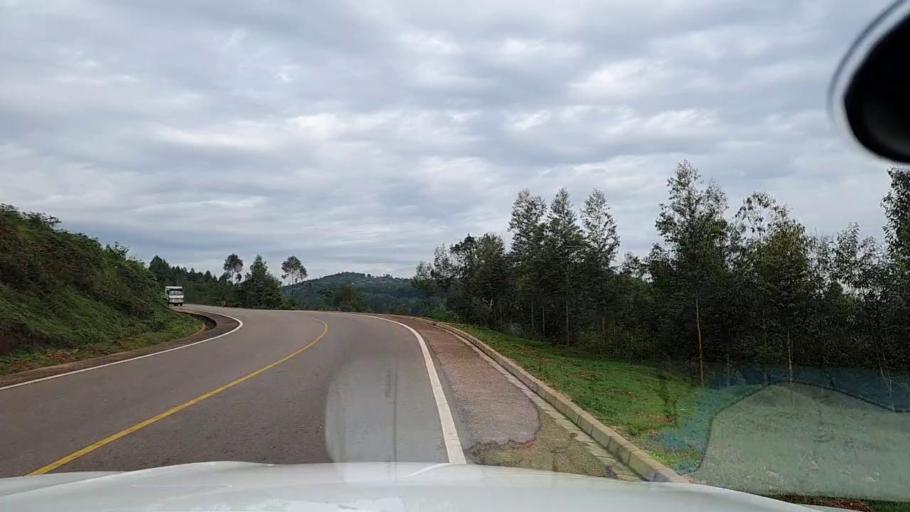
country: RW
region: Southern Province
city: Butare
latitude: -2.5591
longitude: 29.7177
